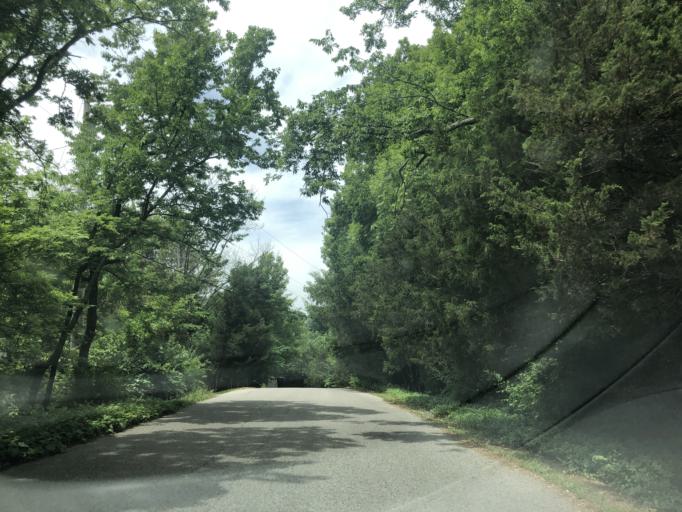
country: US
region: Tennessee
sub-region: Davidson County
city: Oak Hill
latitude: 36.0871
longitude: -86.8088
